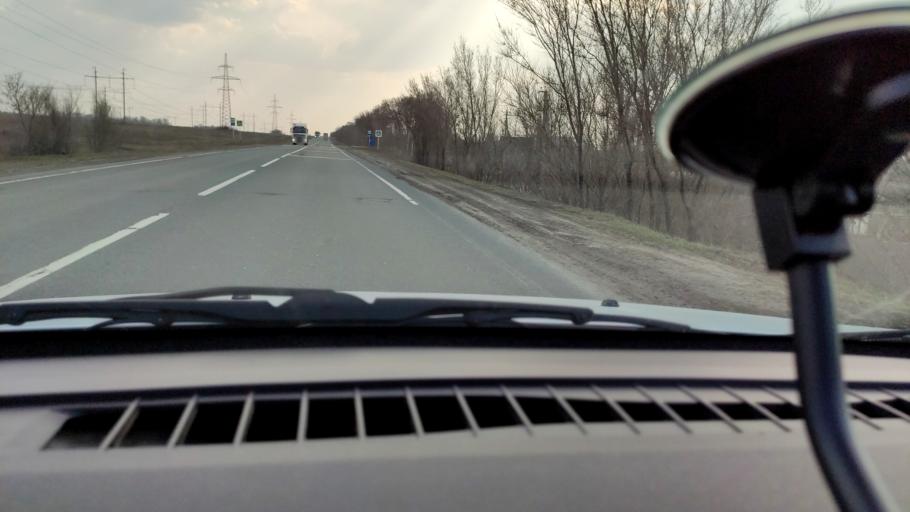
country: RU
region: Samara
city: Dubovyy Umet
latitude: 53.0829
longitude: 50.3914
